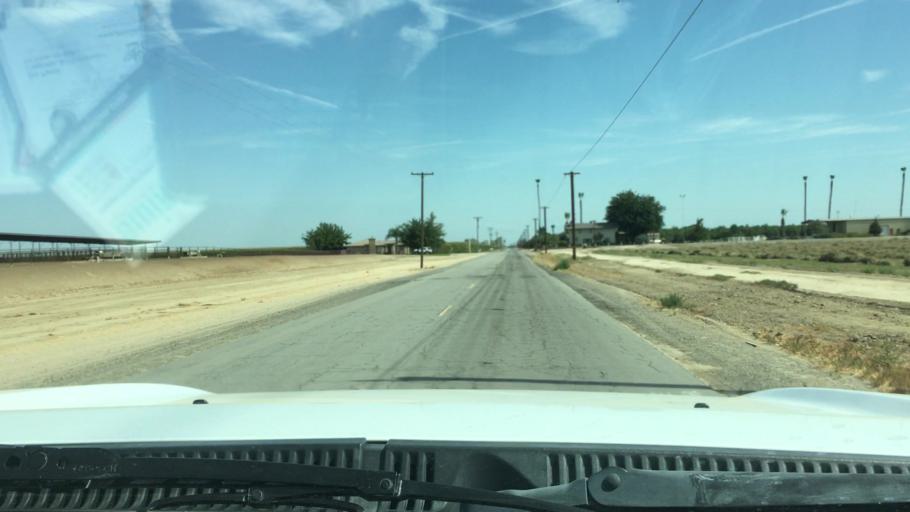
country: US
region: California
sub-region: Kern County
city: Buttonwillow
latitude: 35.4182
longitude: -119.3764
